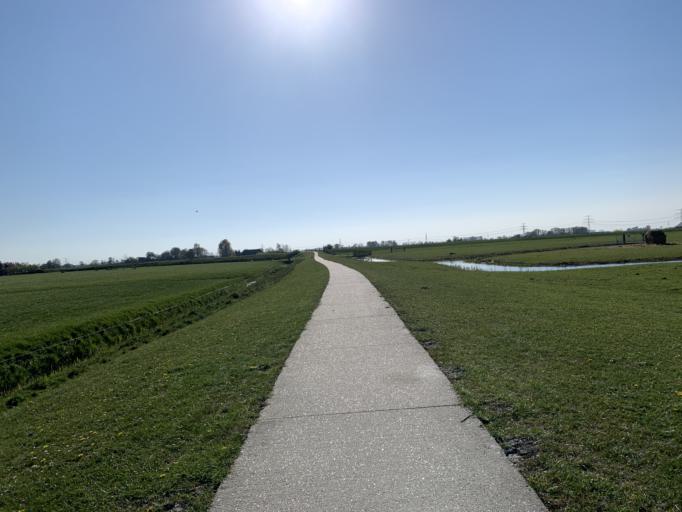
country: NL
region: Groningen
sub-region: Gemeente Winsum
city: Winsum
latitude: 53.2840
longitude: 6.5090
